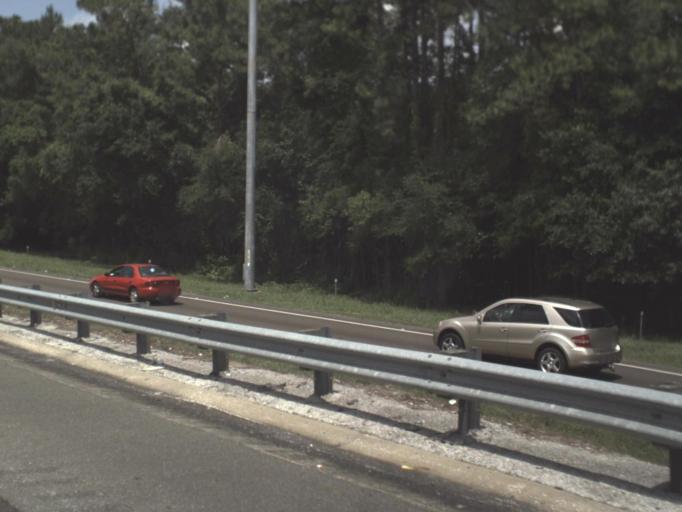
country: US
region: Florida
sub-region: Clay County
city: Bellair-Meadowbrook Terrace
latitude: 30.2501
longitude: -81.7627
